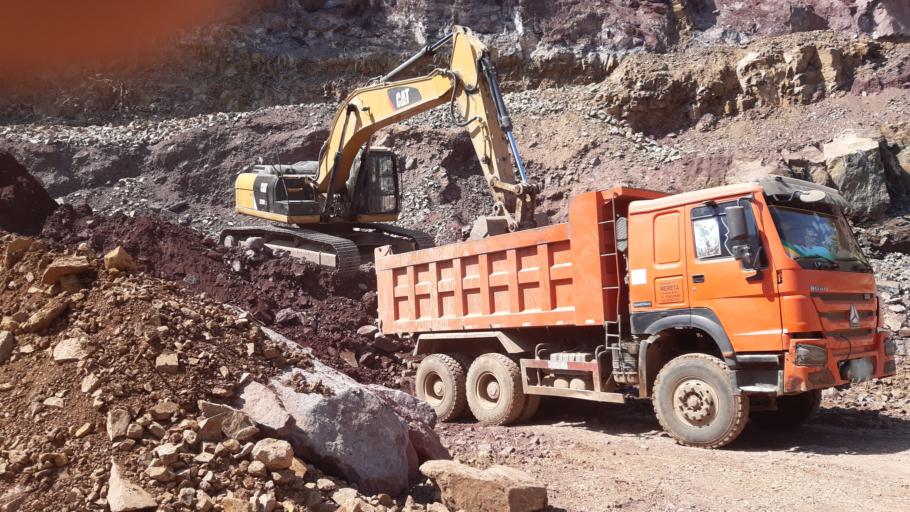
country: ET
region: Amhara
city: Dabat
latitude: 13.1896
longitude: 37.5874
